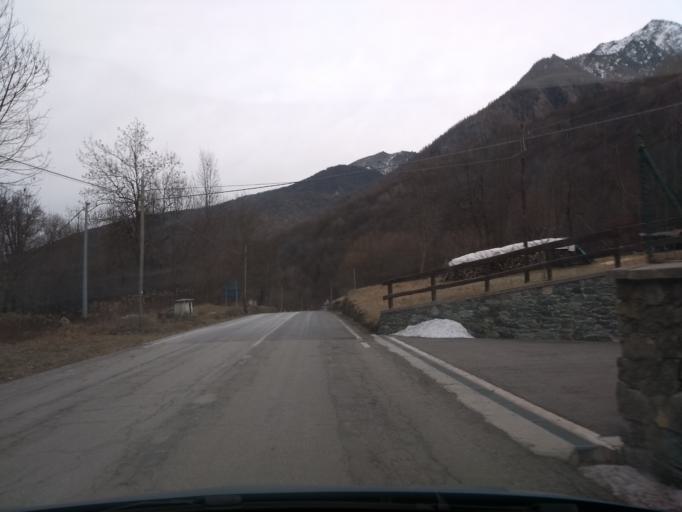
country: IT
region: Piedmont
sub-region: Provincia di Torino
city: Lemie
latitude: 45.2230
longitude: 7.3092
